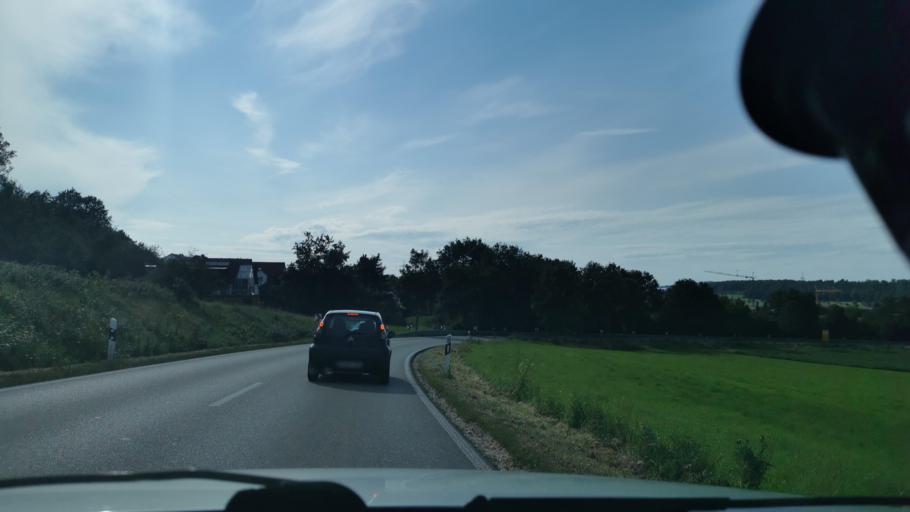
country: DE
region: Baden-Wuerttemberg
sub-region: Regierungsbezirk Stuttgart
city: Schlierbach
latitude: 48.6873
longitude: 9.5054
